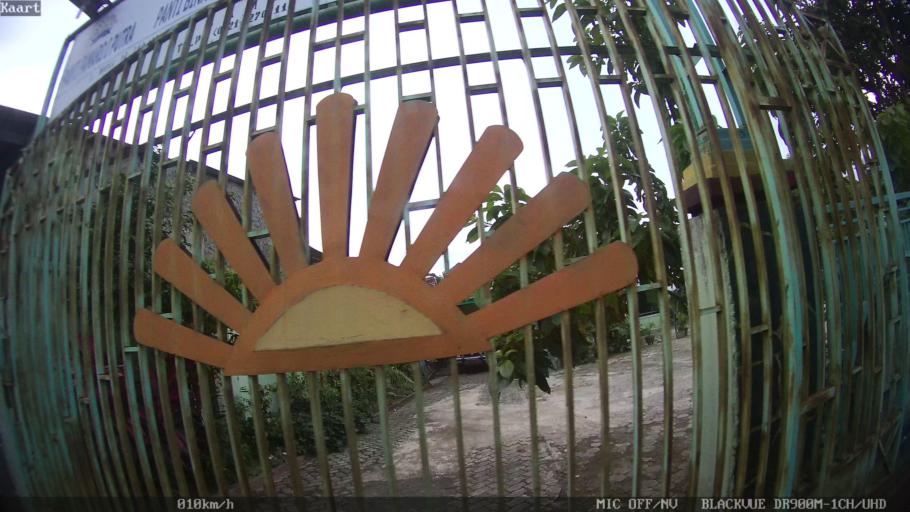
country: ID
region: Lampung
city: Kedaton
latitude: -5.3937
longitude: 105.2020
